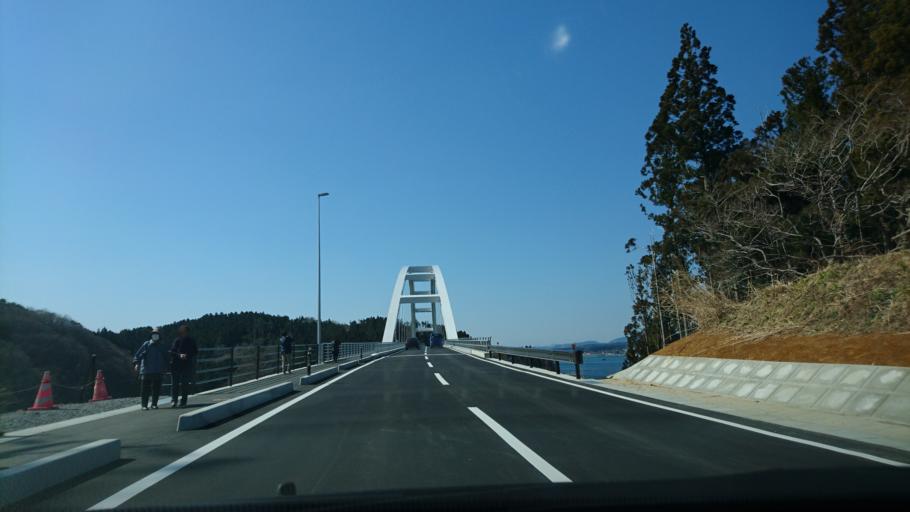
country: JP
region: Iwate
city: Ofunato
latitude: 38.8806
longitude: 141.6071
